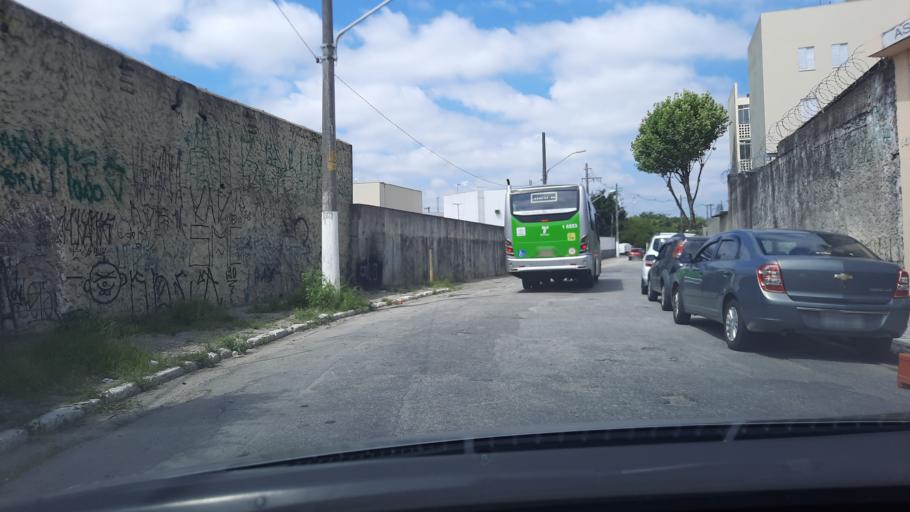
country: BR
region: Sao Paulo
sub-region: Sao Paulo
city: Sao Paulo
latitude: -23.5081
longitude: -46.6845
